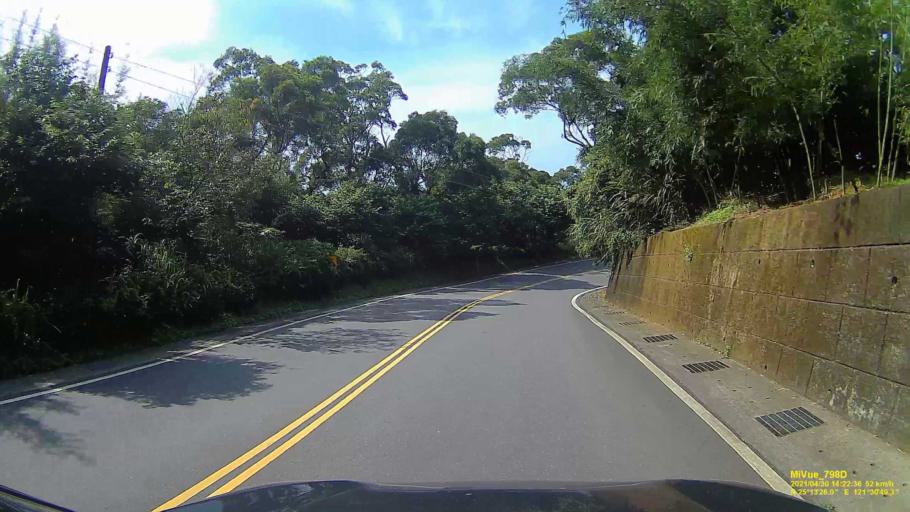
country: TW
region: Taipei
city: Taipei
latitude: 25.2241
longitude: 121.5136
